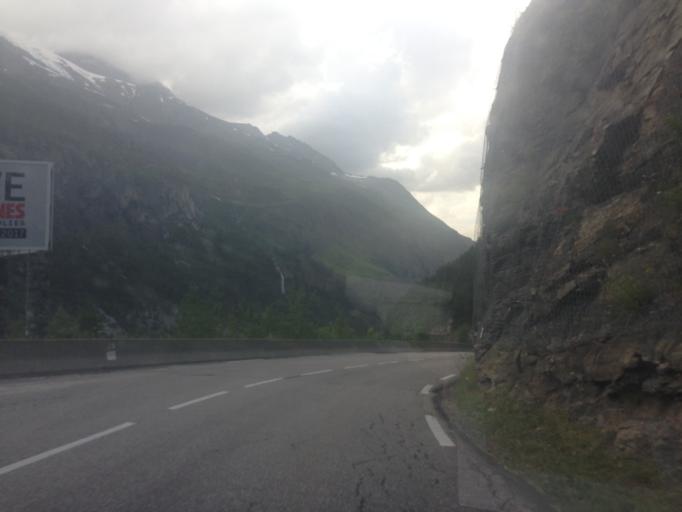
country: FR
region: Rhone-Alpes
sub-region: Departement de la Savoie
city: Tignes
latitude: 45.5073
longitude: 6.9256
